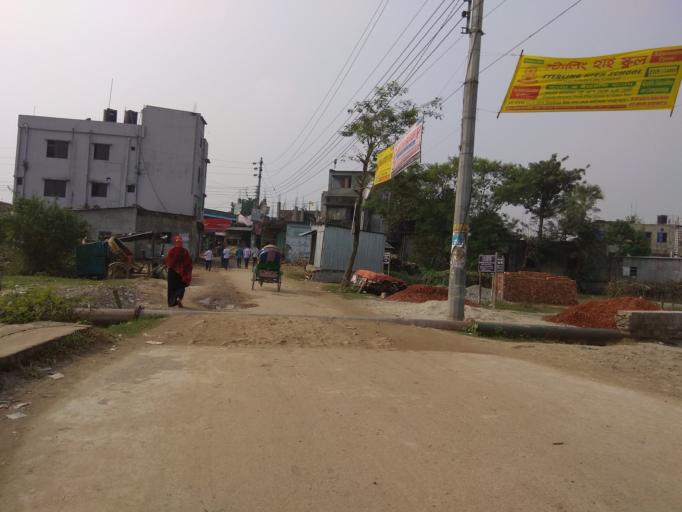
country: BD
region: Dhaka
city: Tungi
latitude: 23.8543
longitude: 90.3789
